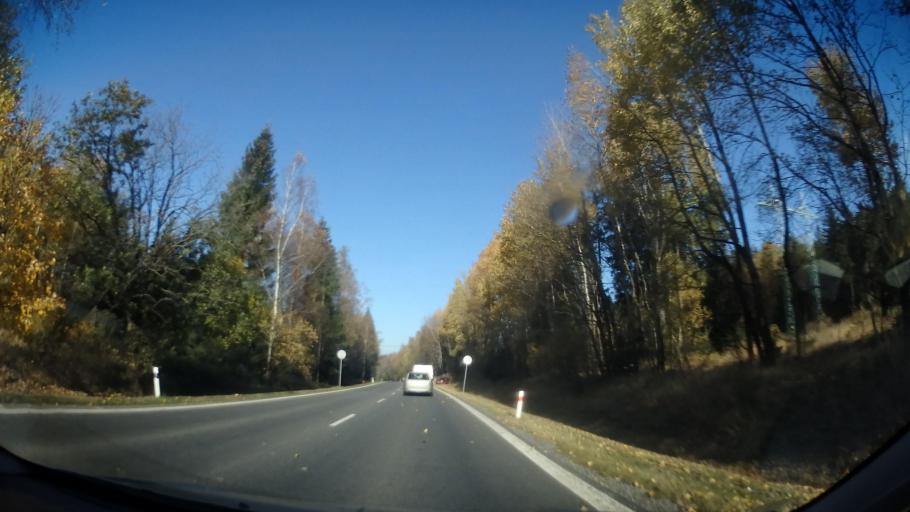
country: CZ
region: Vysocina
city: Krizova
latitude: 49.6656
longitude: 15.9002
